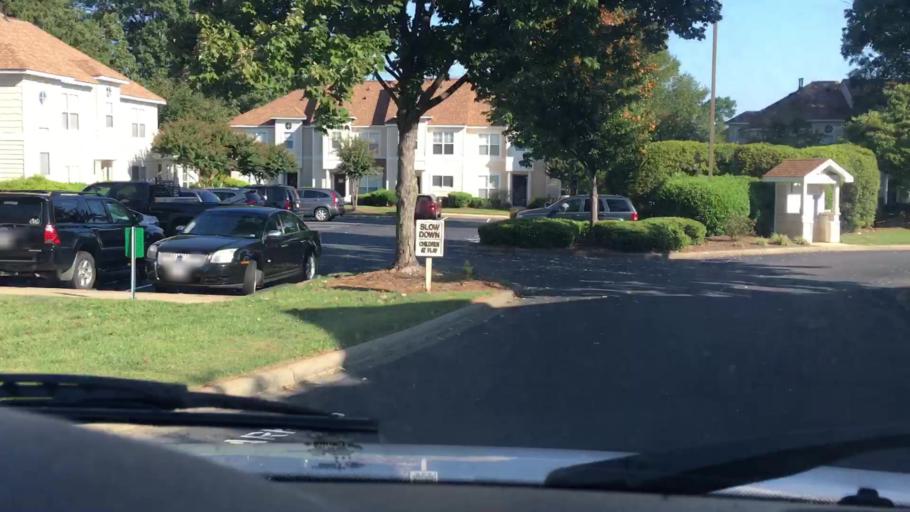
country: US
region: North Carolina
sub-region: Mecklenburg County
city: Cornelius
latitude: 35.4527
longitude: -80.8898
